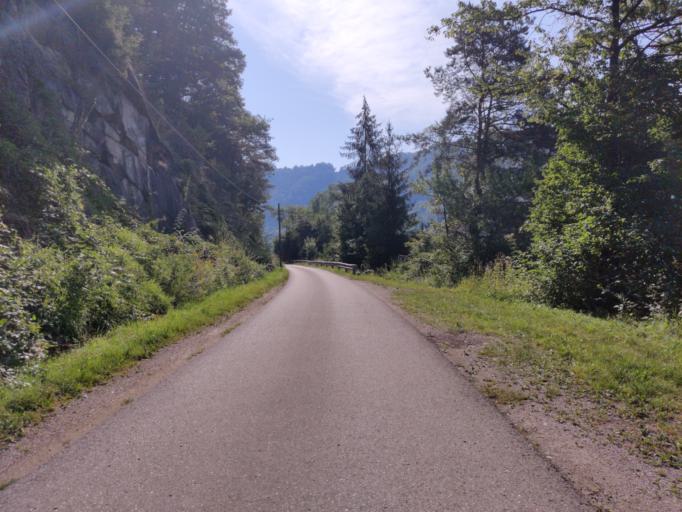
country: AT
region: Upper Austria
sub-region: Politischer Bezirk Rohrbach
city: Kleinzell im Muehlkreis
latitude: 48.4185
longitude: 13.9598
